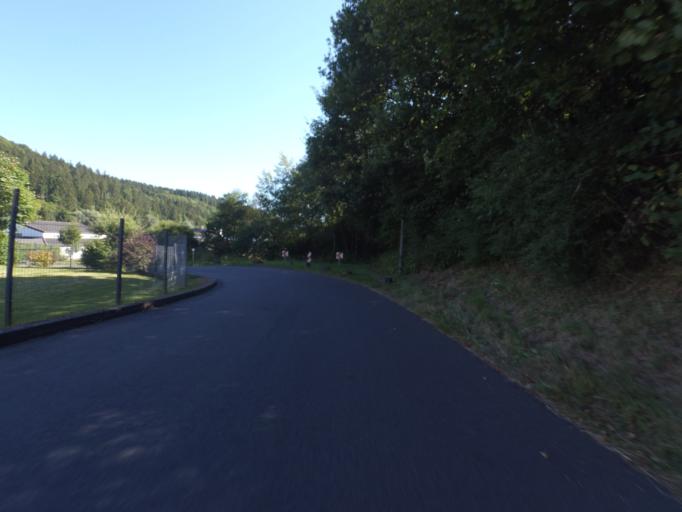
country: DE
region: Rheinland-Pfalz
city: Daun
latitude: 50.2183
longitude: 6.8407
